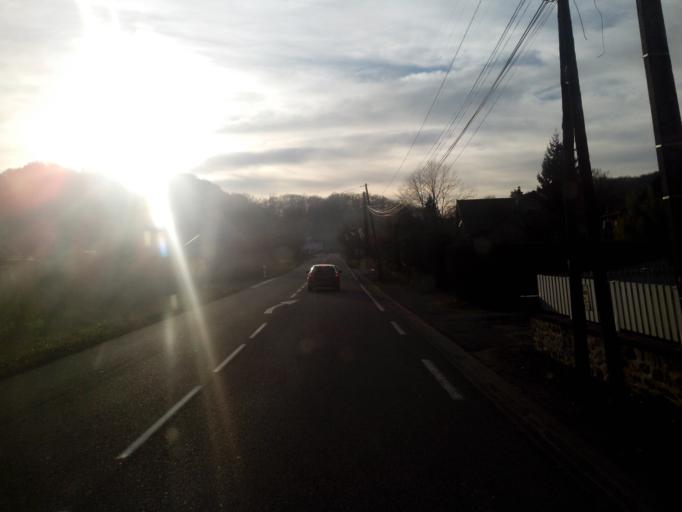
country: FR
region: Limousin
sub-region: Departement de la Correze
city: Bort-les-Orgues
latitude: 45.3778
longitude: 2.4811
